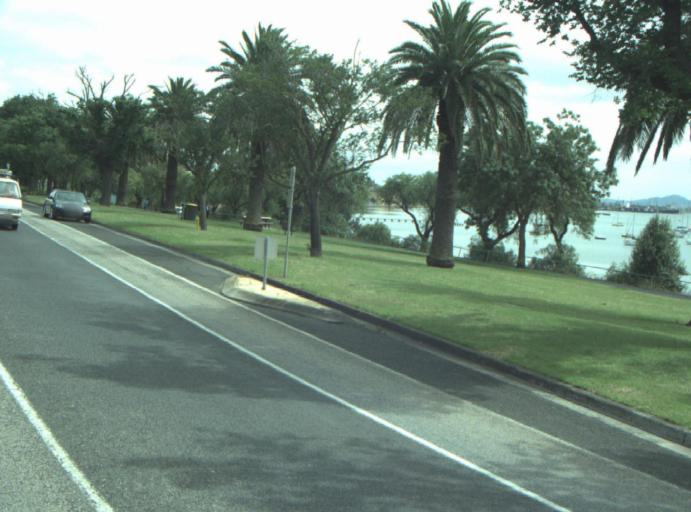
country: AU
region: Victoria
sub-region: Greater Geelong
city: Geelong
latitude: -38.1402
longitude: 144.3567
